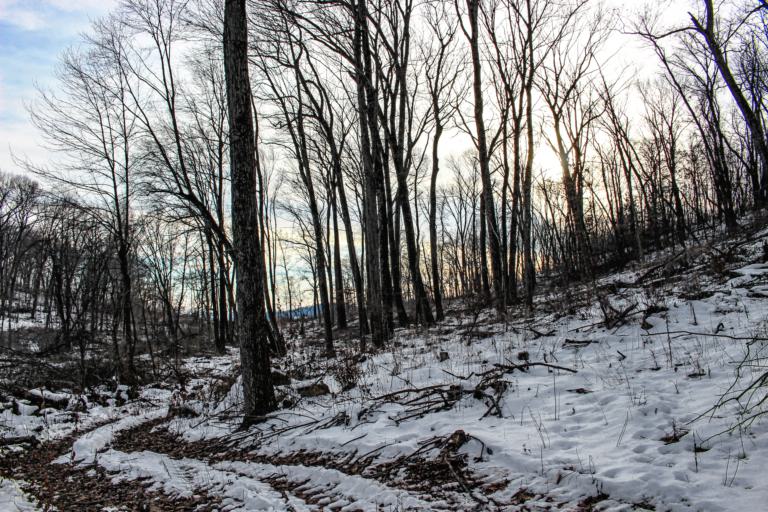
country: US
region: Wisconsin
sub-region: Dane County
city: Deerfield
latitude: 43.0972
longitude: -89.0603
